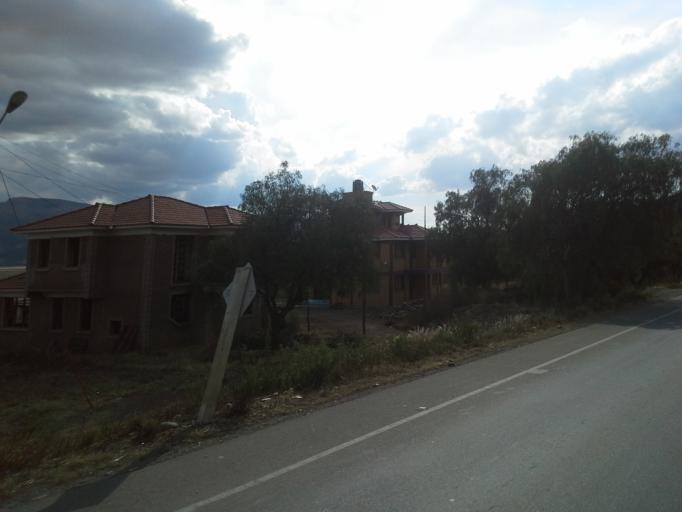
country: BO
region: Cochabamba
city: Tarata
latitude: -17.5419
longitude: -66.0343
